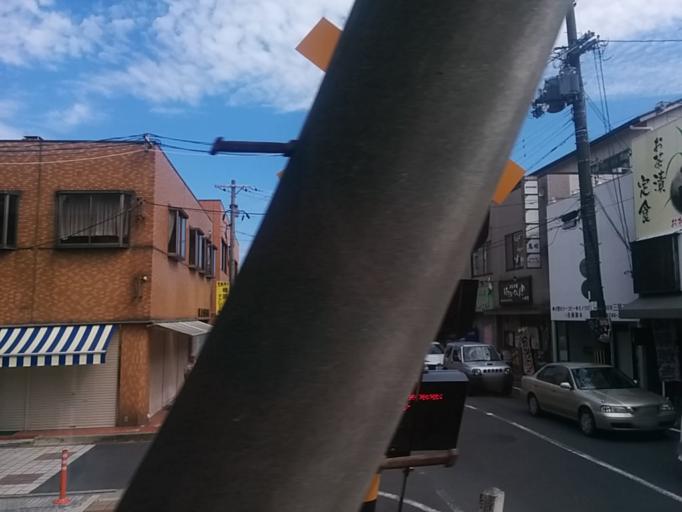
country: JP
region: Nara
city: Kashihara-shi
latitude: 34.5088
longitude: 135.7909
